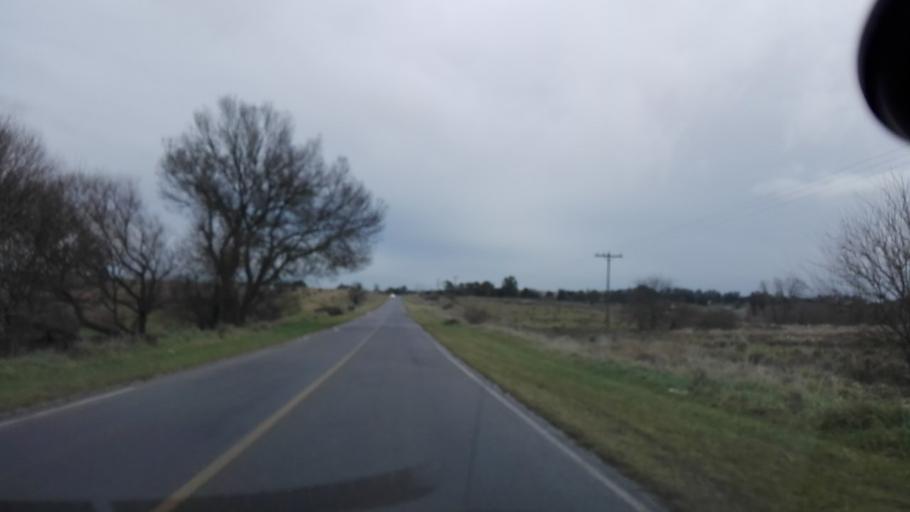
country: AR
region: Buenos Aires
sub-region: Partido de Tandil
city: Tandil
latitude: -37.3555
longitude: -59.1893
